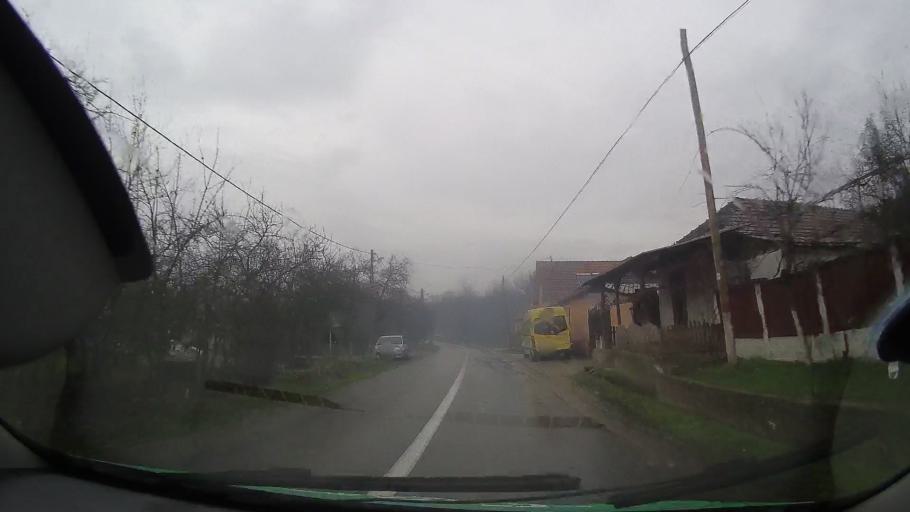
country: RO
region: Bihor
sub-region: Comuna Holod
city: Vintere
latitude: 46.7712
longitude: 22.1378
